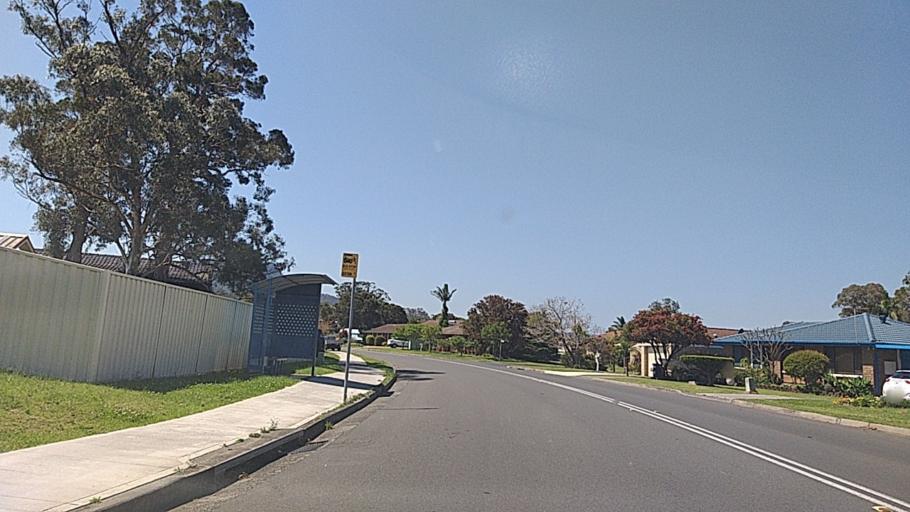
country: AU
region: New South Wales
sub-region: Wollongong
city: Dapto
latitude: -34.4864
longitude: 150.7815
